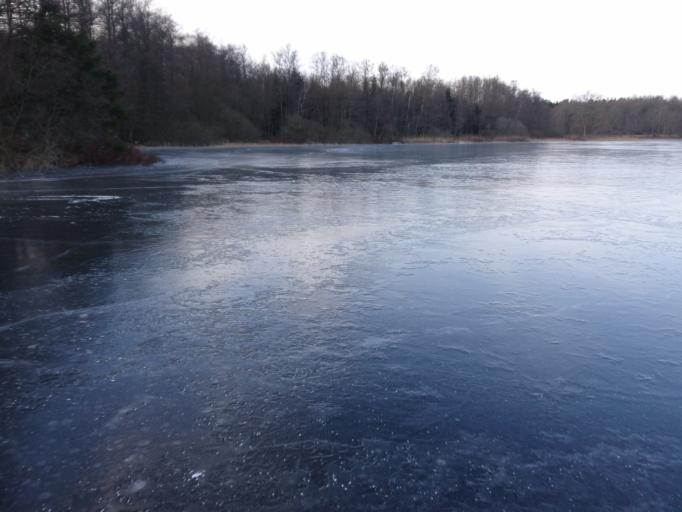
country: SE
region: Blekinge
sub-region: Karlshamns Kommun
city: Karlshamn
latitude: 56.2357
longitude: 14.9663
